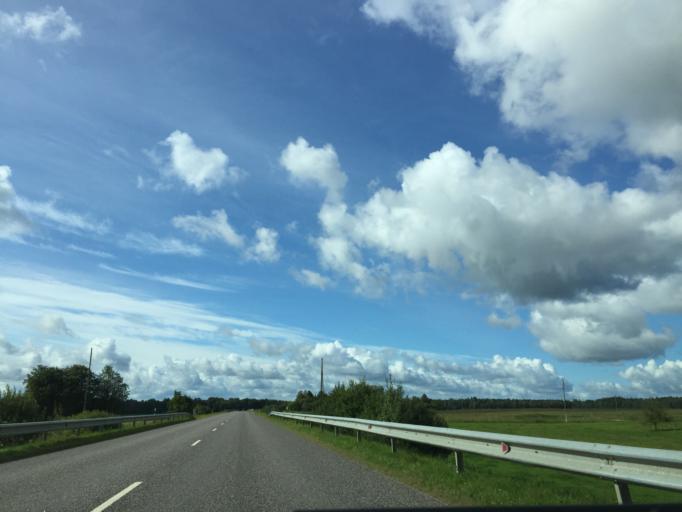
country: LV
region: Kuldigas Rajons
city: Kuldiga
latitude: 57.0015
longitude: 22.1348
